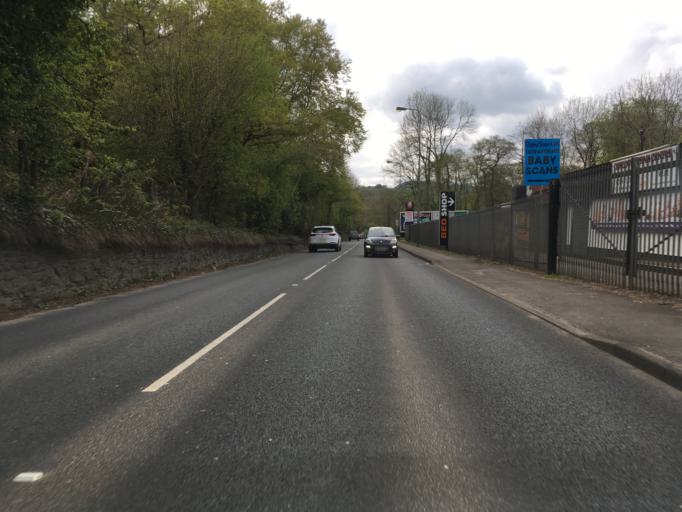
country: GB
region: Wales
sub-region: Merthyr Tydfil County Borough
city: Treharris
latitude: 51.6508
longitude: -3.3053
